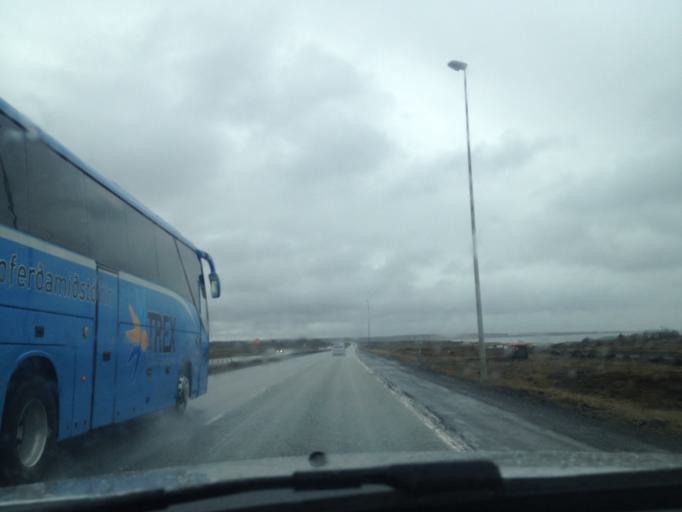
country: IS
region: Capital Region
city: Alftanes
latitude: 64.0197
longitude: -22.1447
